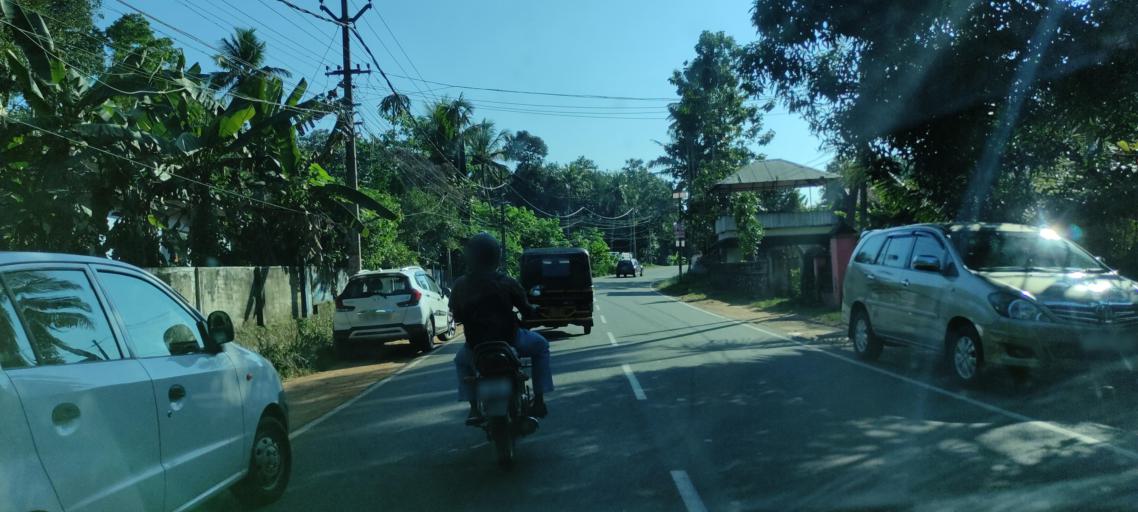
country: IN
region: Kerala
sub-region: Pattanamtitta
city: Pathanamthitta
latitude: 9.2333
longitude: 76.7552
